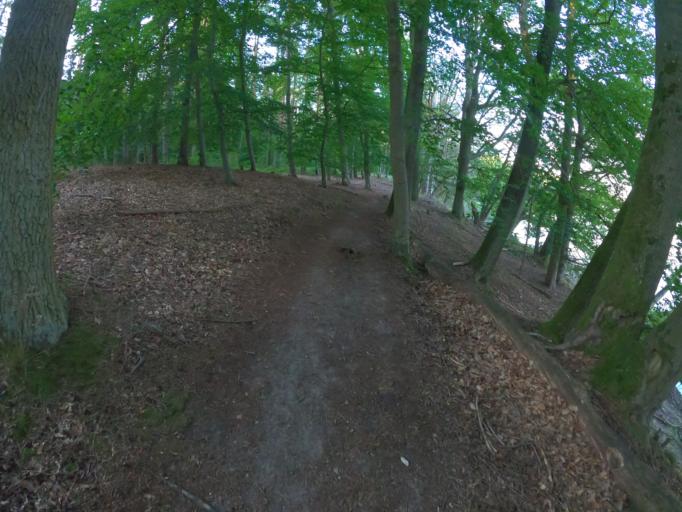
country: DE
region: Brandenburg
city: Angermunde
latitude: 53.0258
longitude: 13.9189
